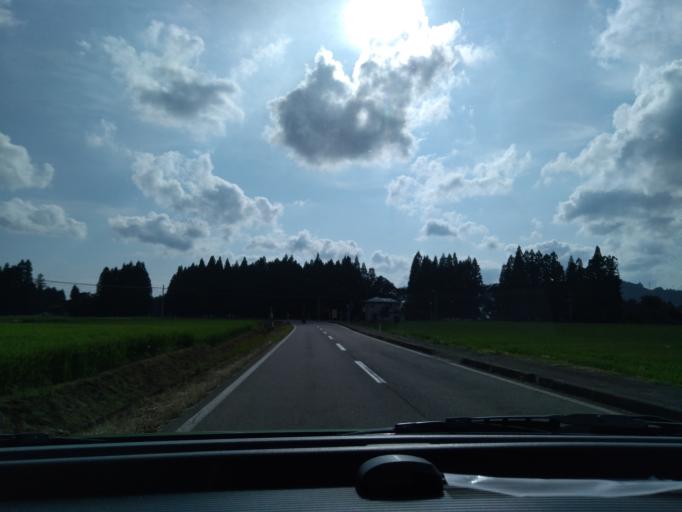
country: JP
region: Akita
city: Kakunodatemachi
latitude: 39.5848
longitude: 140.6020
